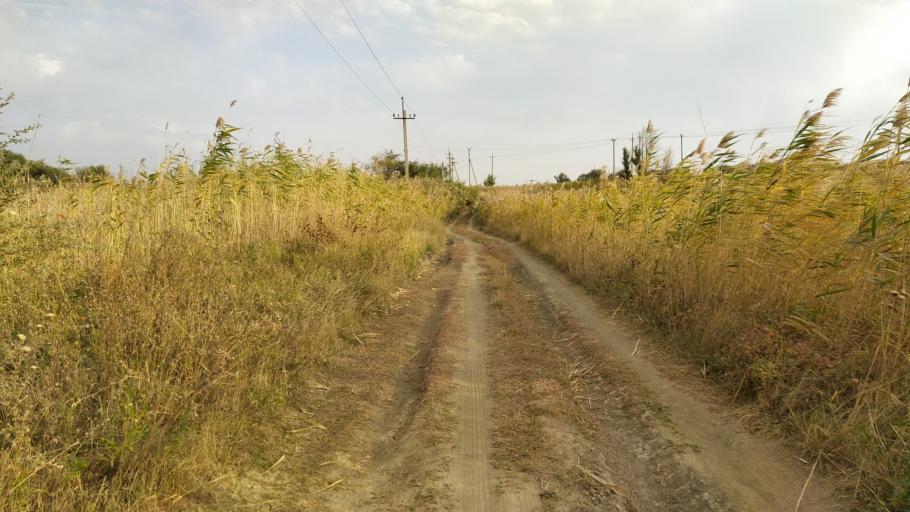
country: RU
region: Rostov
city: Kuleshovka
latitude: 47.1099
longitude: 39.6128
